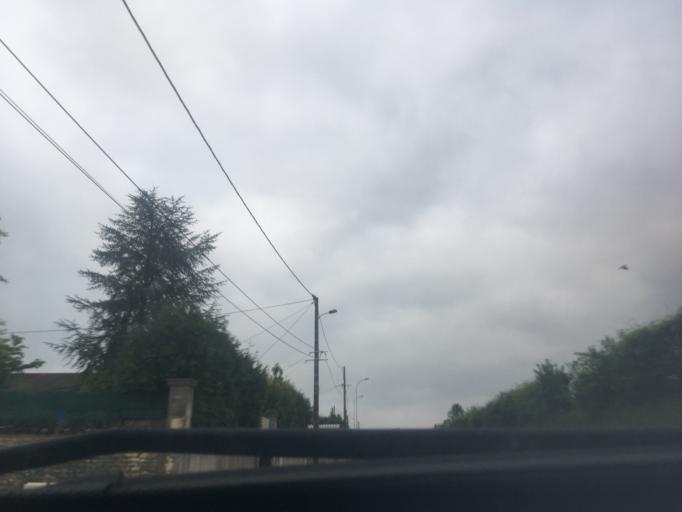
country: FR
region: Poitou-Charentes
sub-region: Departement de la Charente
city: Chateaubernard
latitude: 45.6807
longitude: -0.3338
